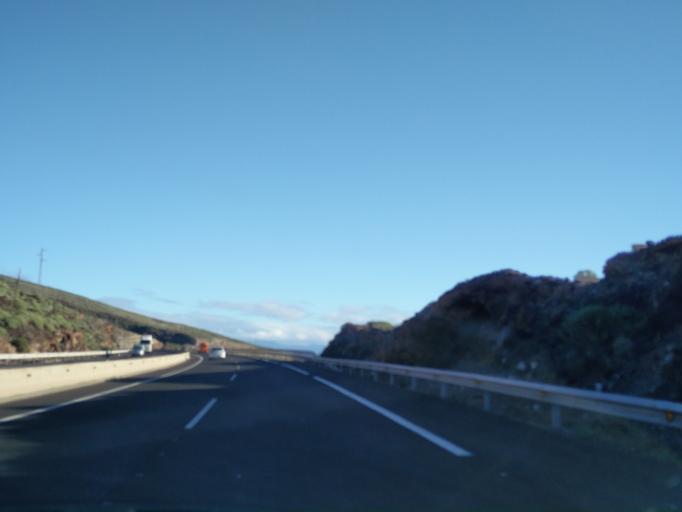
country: ES
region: Canary Islands
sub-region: Provincia de Santa Cruz de Tenerife
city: Fasnia
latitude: 28.2523
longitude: -16.3976
